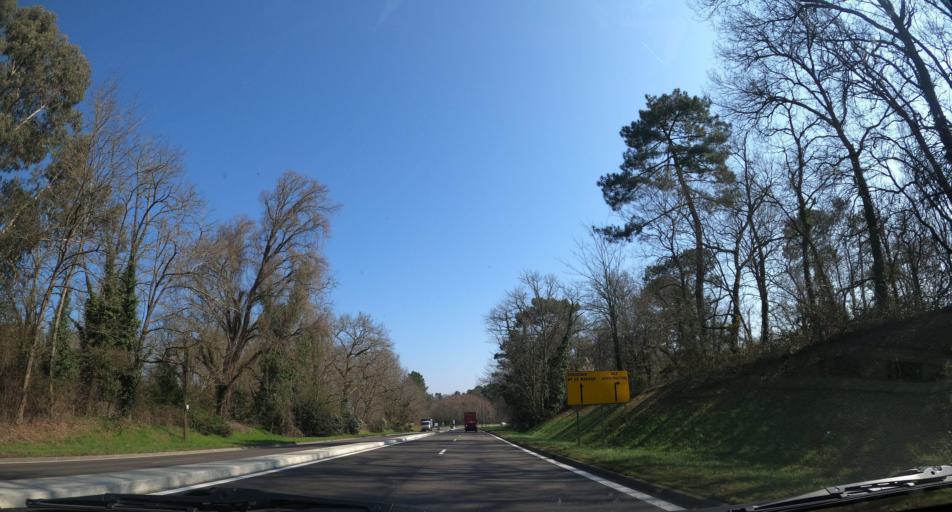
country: FR
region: Aquitaine
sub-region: Departement des Landes
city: Saint-Pierre-du-Mont
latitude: 43.8823
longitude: -0.5328
